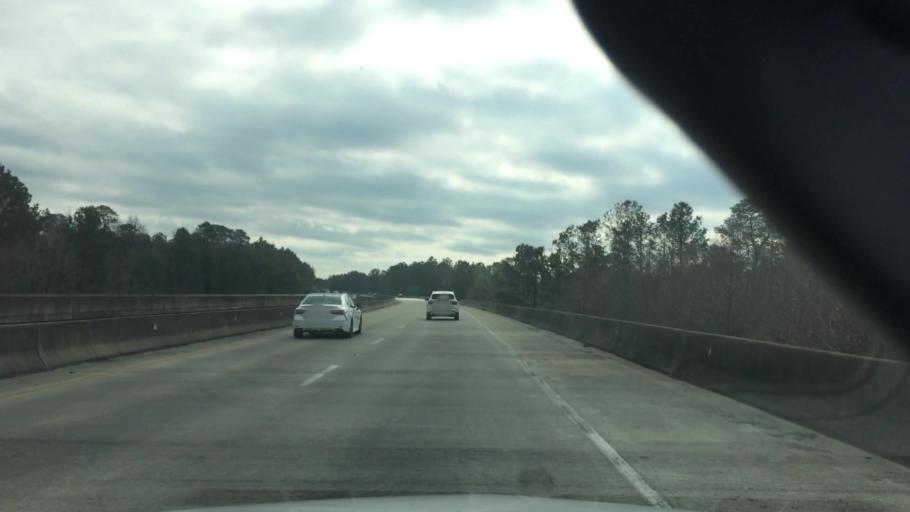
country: US
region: North Carolina
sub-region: New Hanover County
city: Castle Hayne
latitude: 34.3659
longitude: -77.8884
